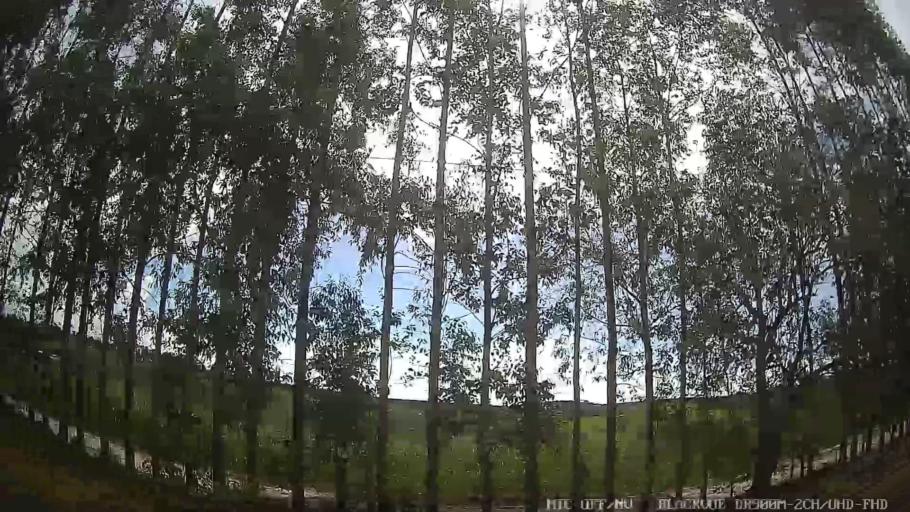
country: BR
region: Sao Paulo
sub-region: Conchas
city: Conchas
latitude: -22.9566
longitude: -47.9832
